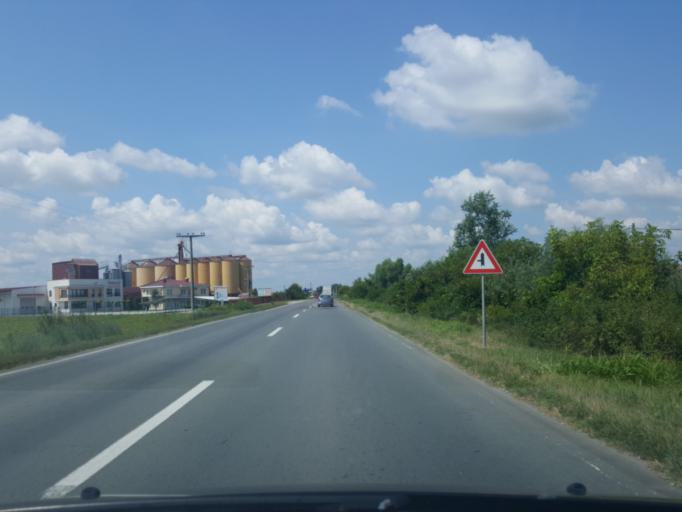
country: RS
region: Autonomna Pokrajina Vojvodina
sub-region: Sremski Okrug
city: Sremska Mitrovica
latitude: 44.9518
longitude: 19.6166
